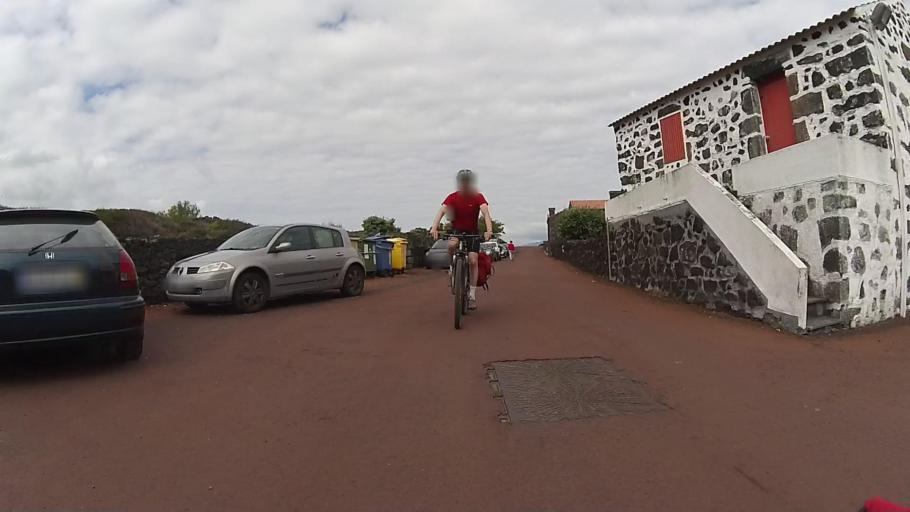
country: PT
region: Azores
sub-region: Madalena
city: Madalena
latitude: 38.5570
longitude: -28.4285
